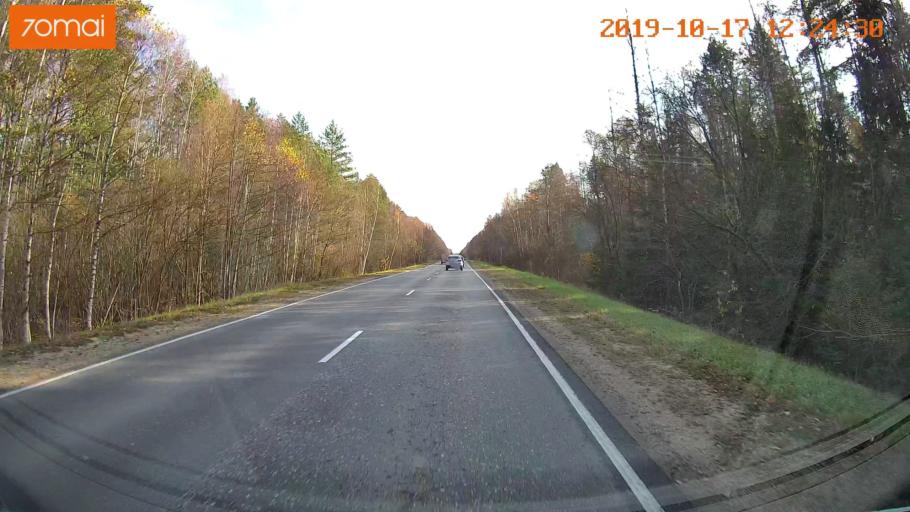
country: RU
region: Rjazan
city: Gus'-Zheleznyy
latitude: 55.0350
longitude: 41.2161
